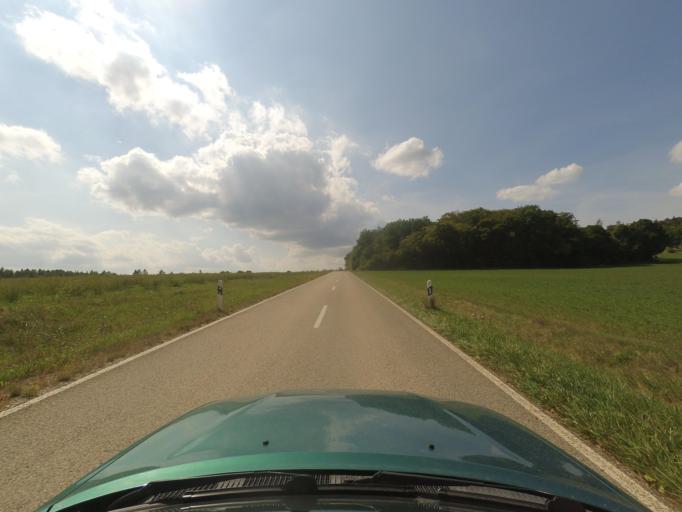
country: DE
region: Bavaria
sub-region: Regierungsbezirk Mittelfranken
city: Raitenbuch
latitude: 49.0198
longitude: 11.1711
